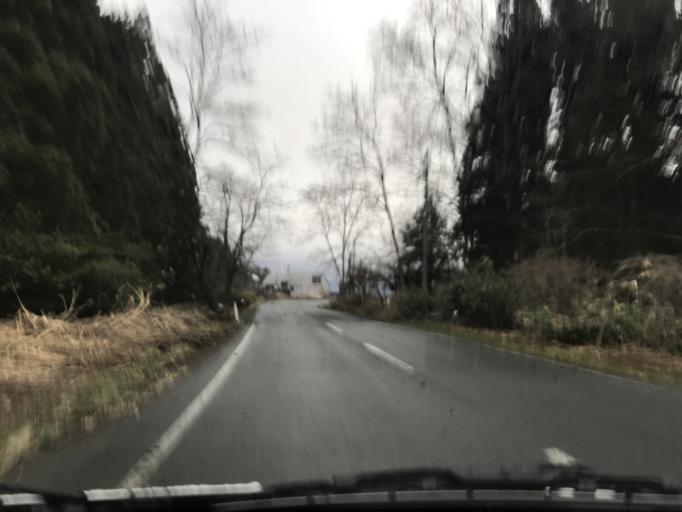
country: JP
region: Iwate
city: Mizusawa
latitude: 39.2003
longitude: 141.0877
